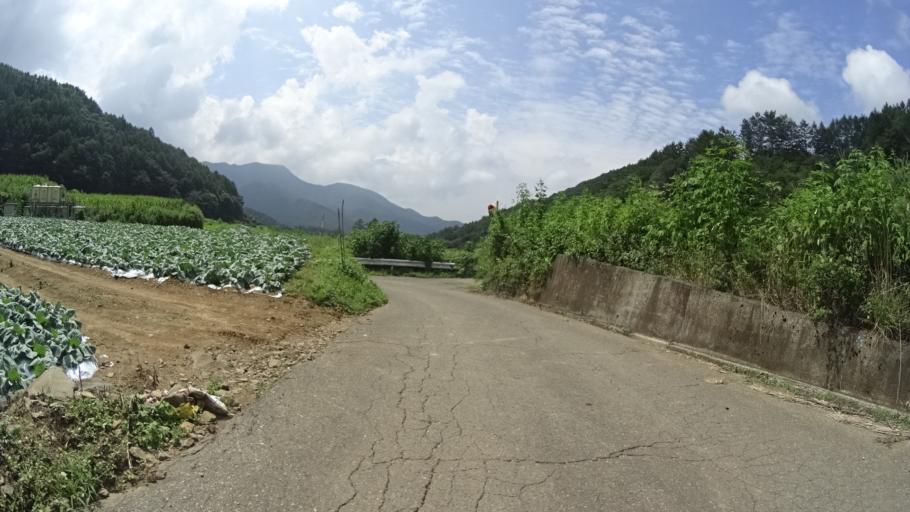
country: JP
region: Yamanashi
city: Nirasaki
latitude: 35.9020
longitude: 138.4705
